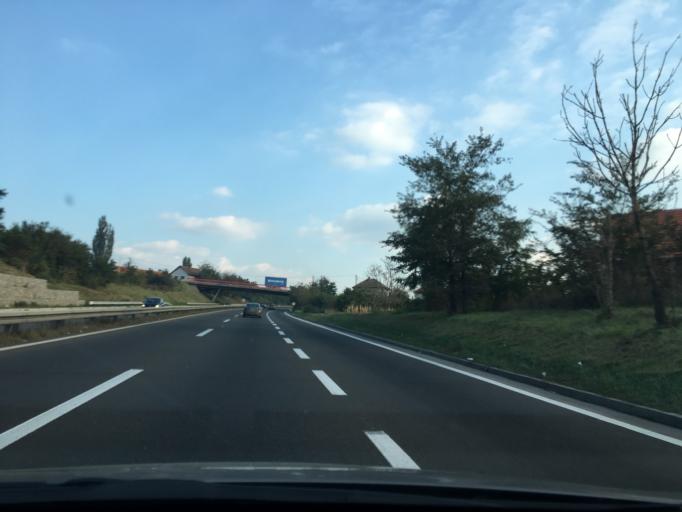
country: RS
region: Central Serbia
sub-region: Belgrade
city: Zvezdara
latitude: 44.7634
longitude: 20.5296
